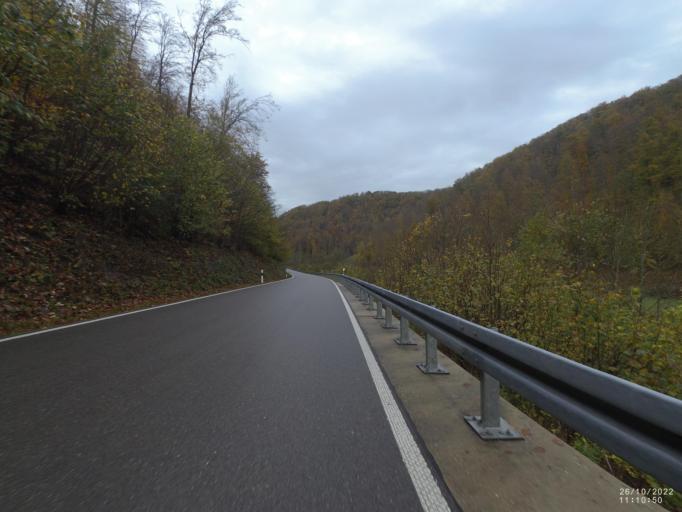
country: DE
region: Baden-Wuerttemberg
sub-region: Regierungsbezirk Stuttgart
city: Bohmenkirch
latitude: 48.6616
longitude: 9.8938
